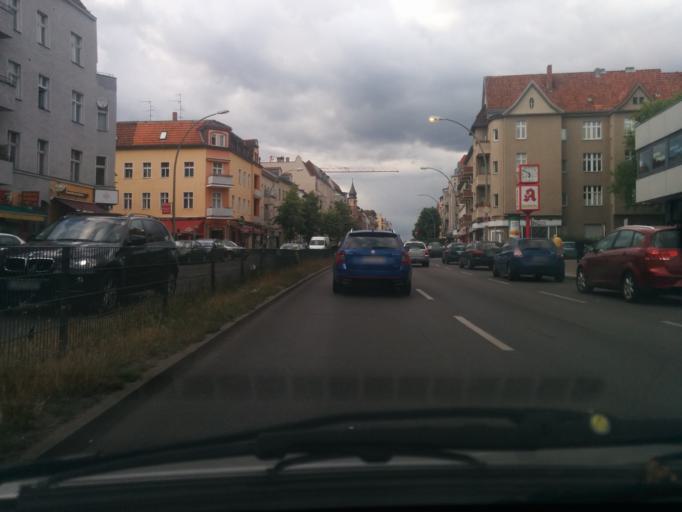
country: DE
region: Berlin
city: Mariendorf
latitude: 52.4565
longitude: 13.3839
